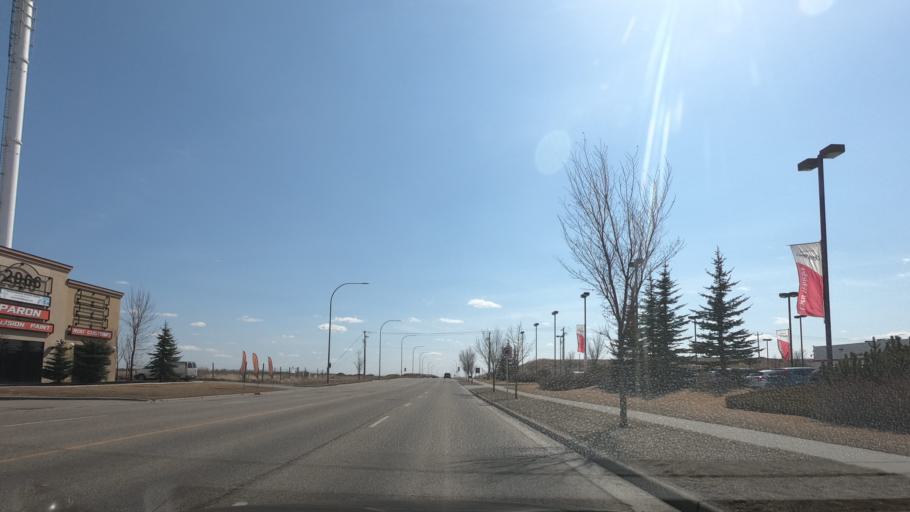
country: CA
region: Alberta
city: Airdrie
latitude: 51.2585
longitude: -114.0051
